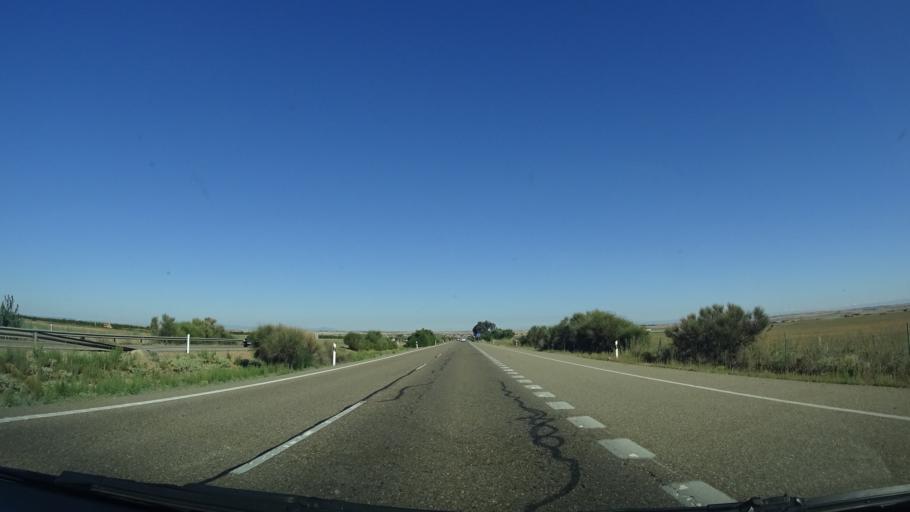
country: ES
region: Castille and Leon
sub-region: Provincia de Zamora
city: Villalpando
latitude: 41.8307
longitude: -5.3813
